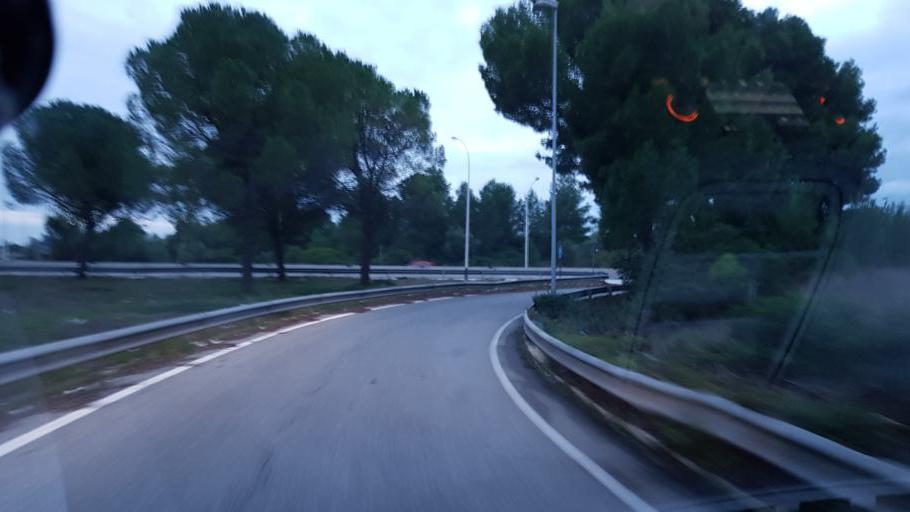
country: IT
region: Apulia
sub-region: Provincia di Taranto
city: Paolo VI
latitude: 40.5125
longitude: 17.2909
